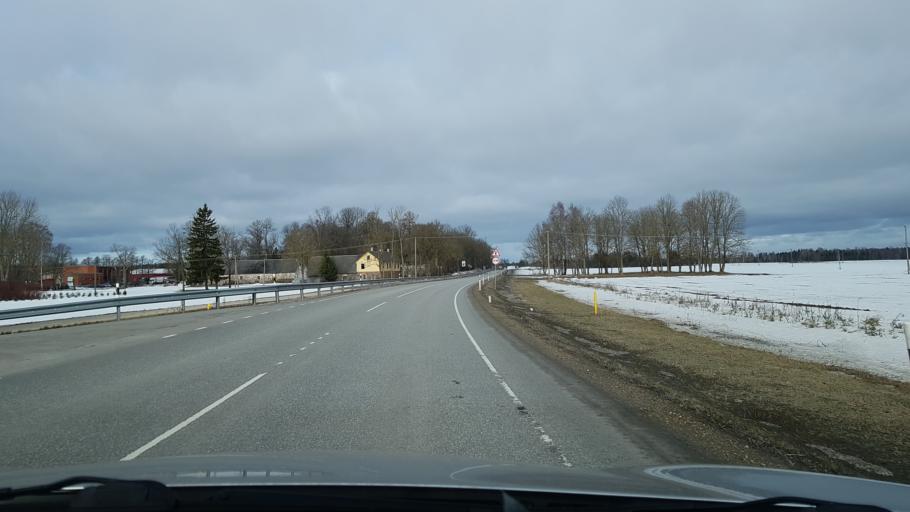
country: EE
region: Jogevamaa
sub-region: Jogeva linn
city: Jogeva
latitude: 58.7566
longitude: 26.3369
